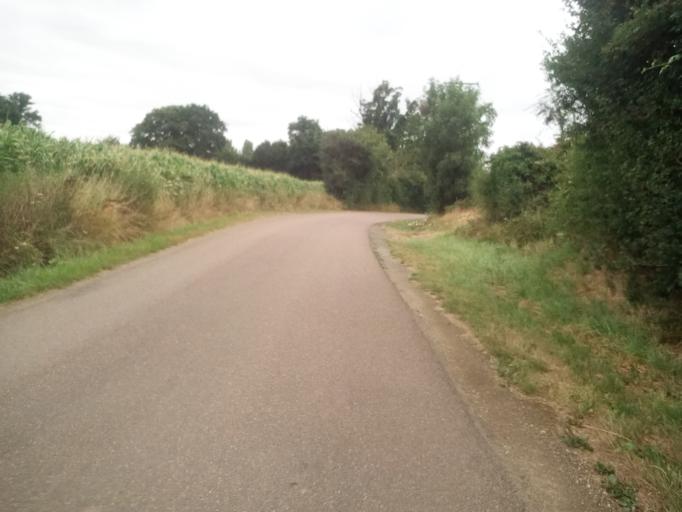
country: FR
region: Lower Normandy
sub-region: Departement du Calvados
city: Clinchamps-sur-Orne
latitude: 49.0398
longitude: -0.3937
